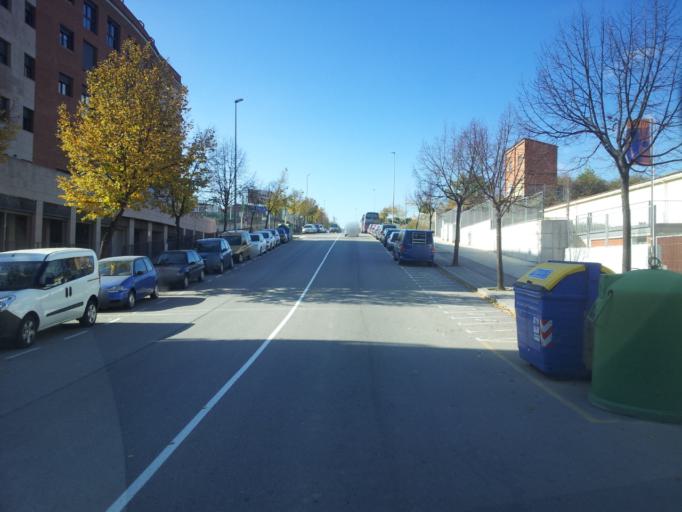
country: ES
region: Catalonia
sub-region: Provincia de Barcelona
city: Vic
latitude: 41.9333
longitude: 2.2418
